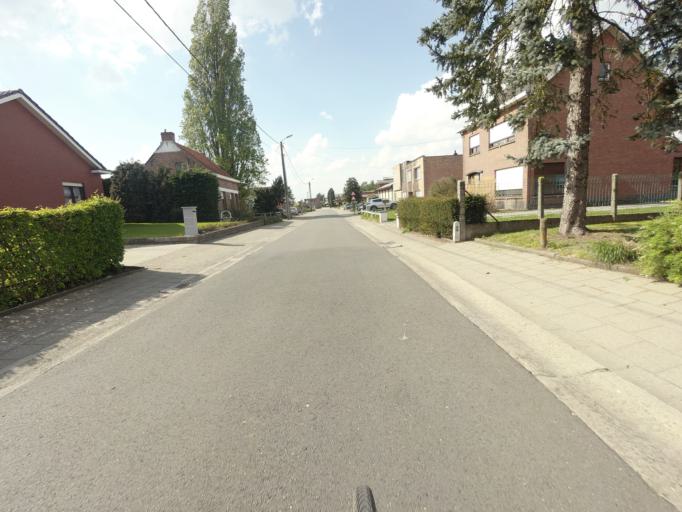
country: BE
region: Flanders
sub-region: Provincie Antwerpen
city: Putte
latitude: 51.0634
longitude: 4.6599
